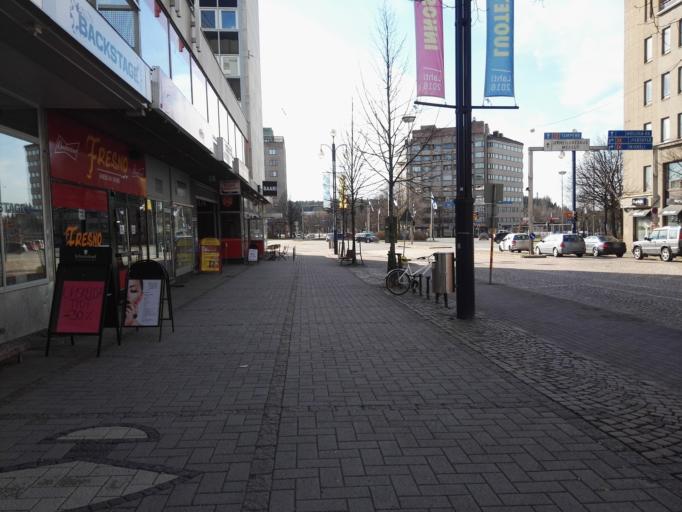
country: FI
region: Paijanne Tavastia
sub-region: Lahti
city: Lahti
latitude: 60.9835
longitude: 25.6522
